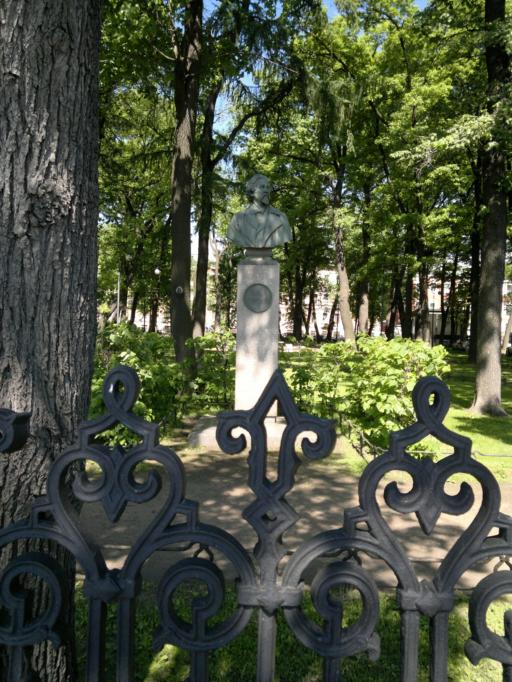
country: RU
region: St.-Petersburg
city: Saint Petersburg
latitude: 59.9378
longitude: 30.2926
